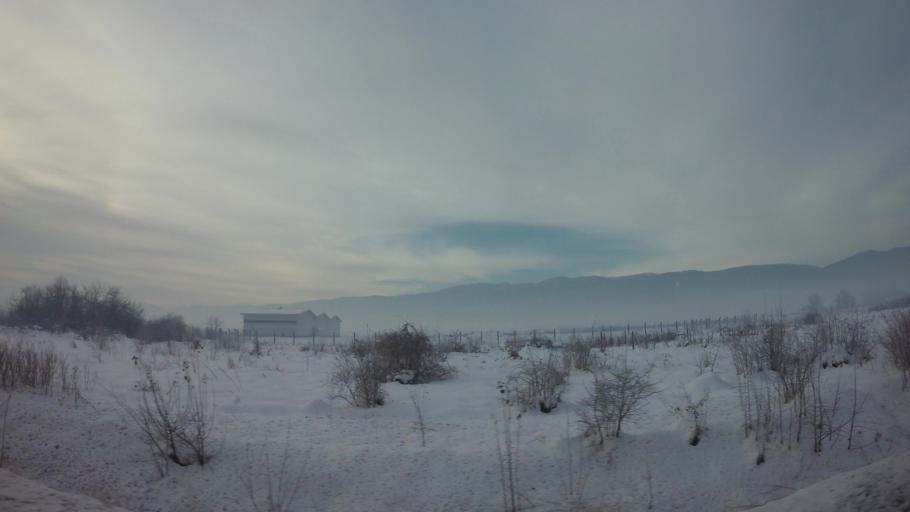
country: BA
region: Federation of Bosnia and Herzegovina
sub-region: Kanton Sarajevo
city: Sarajevo
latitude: 43.8244
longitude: 18.3459
